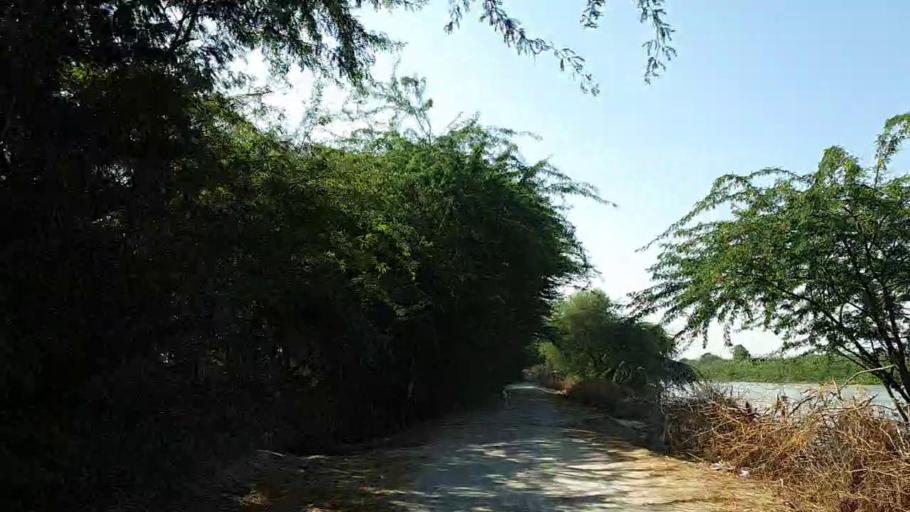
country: PK
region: Sindh
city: Chuhar Jamali
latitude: 24.5731
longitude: 68.0442
